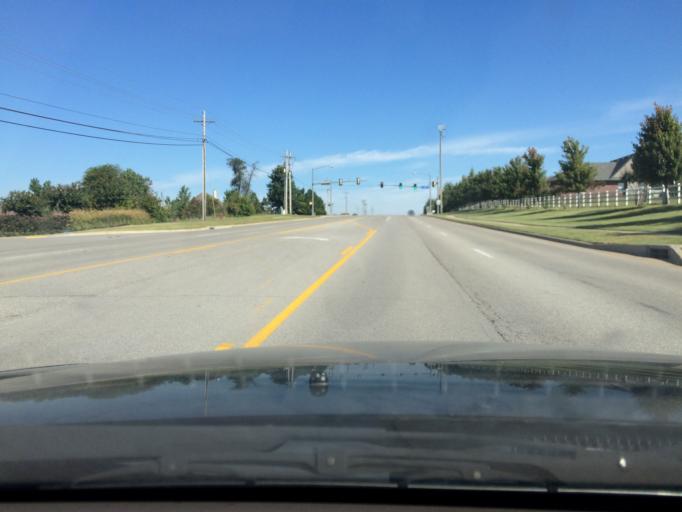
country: US
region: Oklahoma
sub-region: Tulsa County
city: Broken Arrow
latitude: 36.0777
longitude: -95.7974
